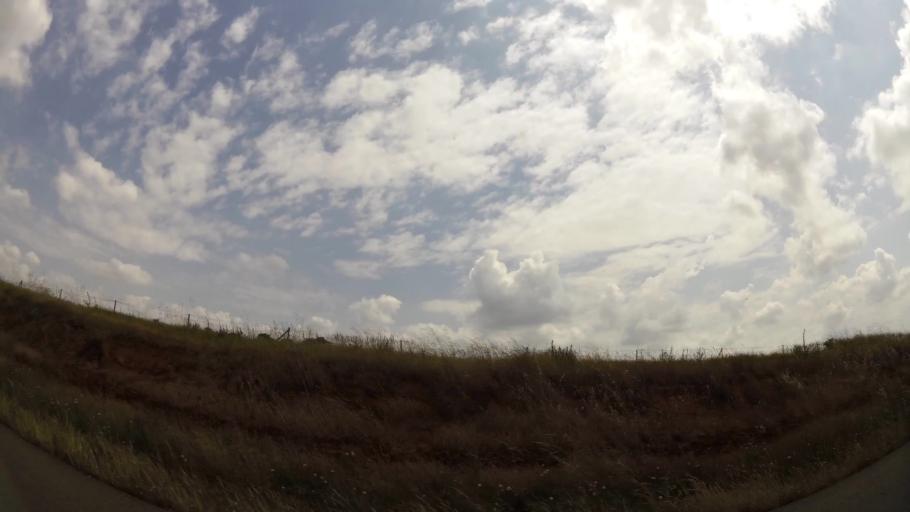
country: MA
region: Rabat-Sale-Zemmour-Zaer
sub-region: Khemisset
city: Tiflet
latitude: 33.9912
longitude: -6.5385
